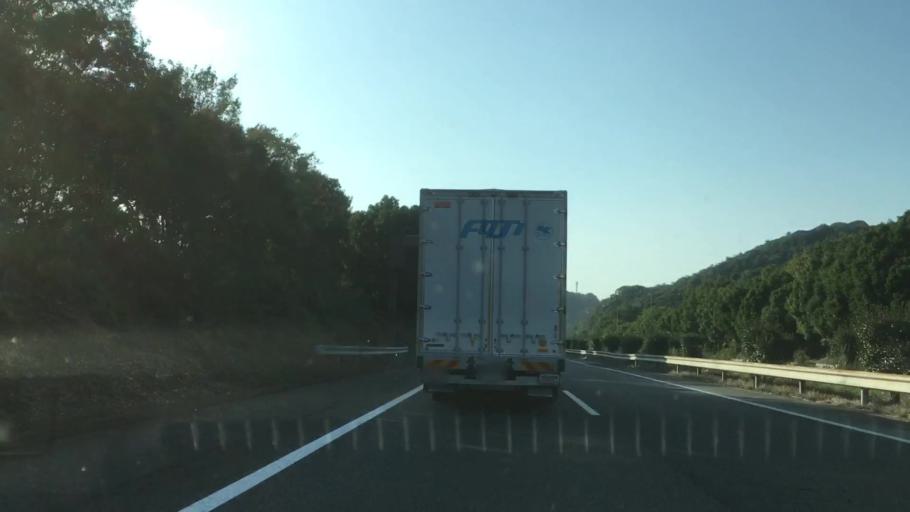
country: JP
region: Yamaguchi
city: Ogori-shimogo
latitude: 34.0848
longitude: 131.4723
